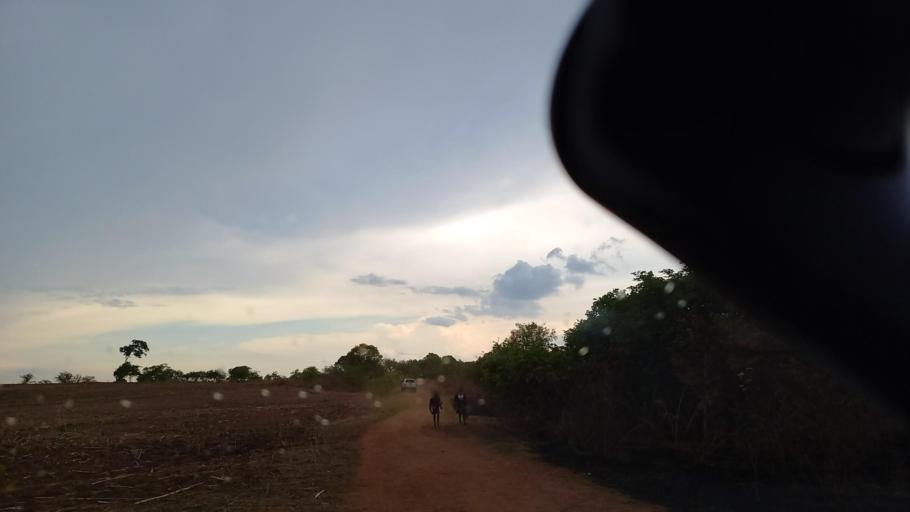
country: ZM
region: Lusaka
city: Kafue
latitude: -15.9880
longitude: 28.2682
